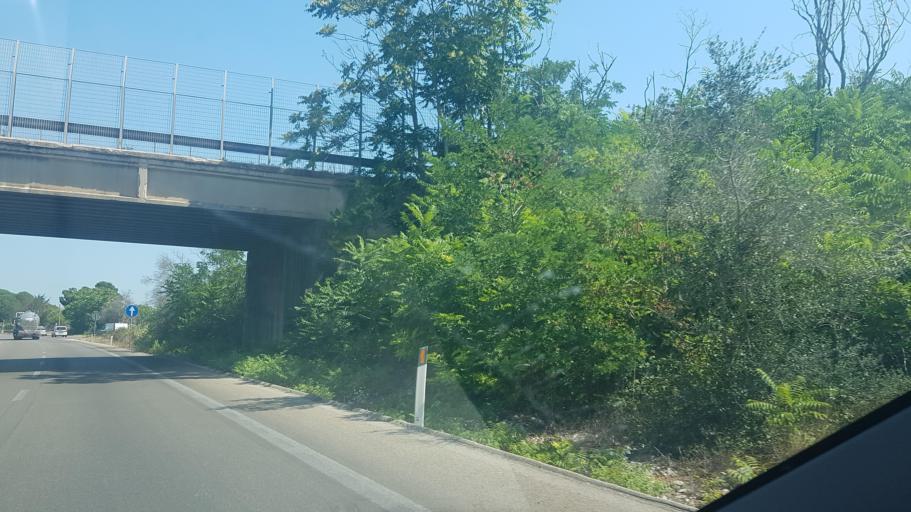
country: IT
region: Apulia
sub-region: Provincia di Lecce
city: Muro Leccese
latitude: 40.1165
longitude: 18.3208
